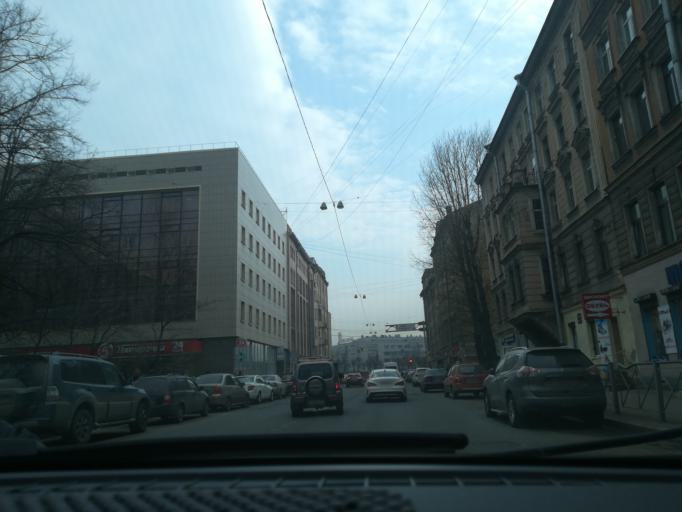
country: RU
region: St.-Petersburg
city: Admiralteisky
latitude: 59.9031
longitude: 30.2737
